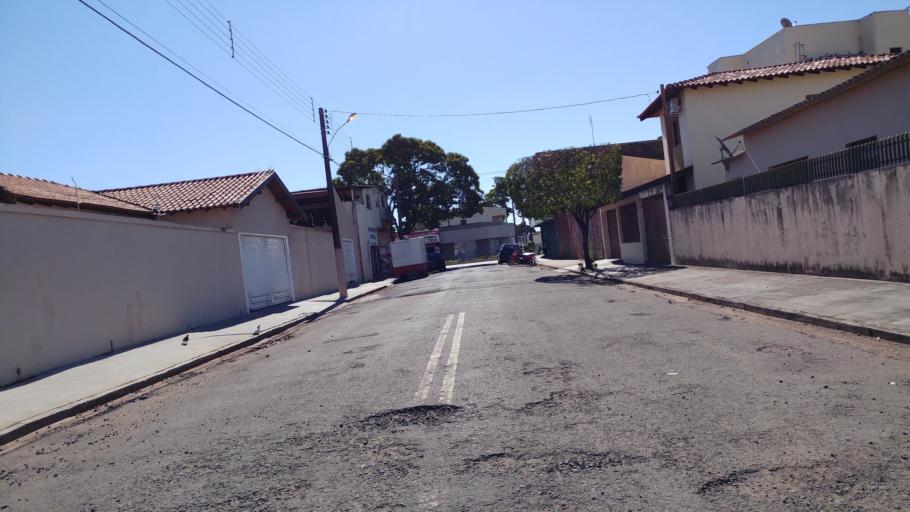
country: BR
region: Sao Paulo
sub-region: Paraguacu Paulista
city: Paraguacu Paulista
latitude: -22.4227
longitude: -50.5806
